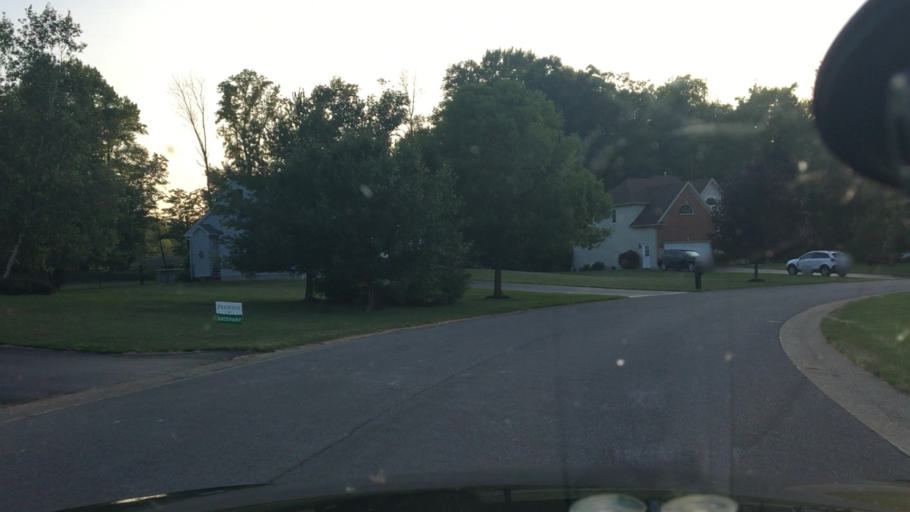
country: US
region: New York
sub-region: Erie County
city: Orchard Park
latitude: 42.7856
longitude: -78.7401
